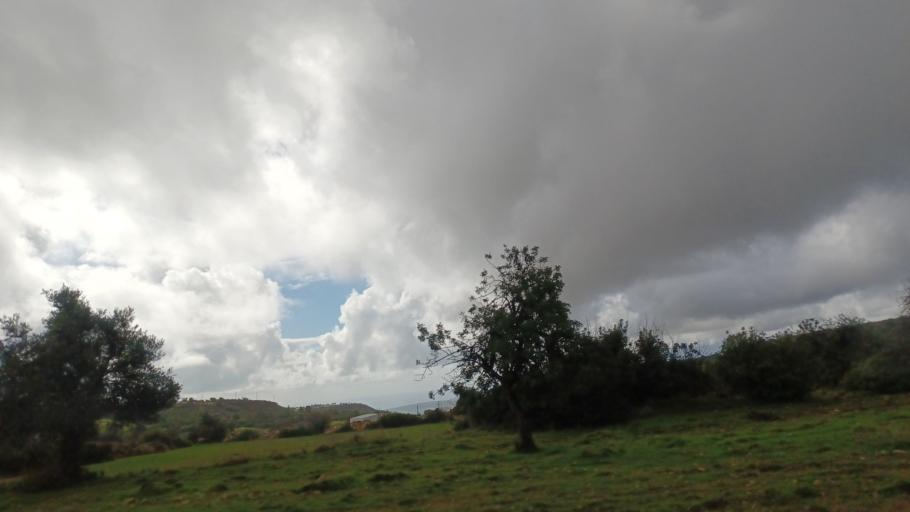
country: CY
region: Limassol
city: Sotira
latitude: 34.7486
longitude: 32.8409
